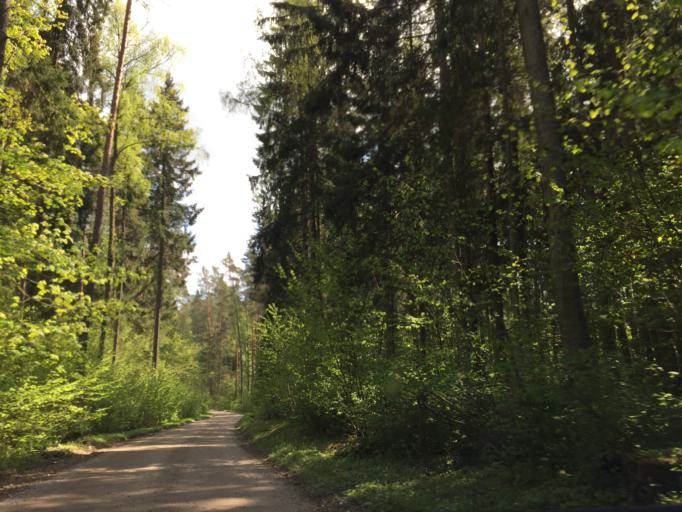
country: LV
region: Ligatne
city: Ligatne
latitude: 57.2943
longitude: 24.9310
